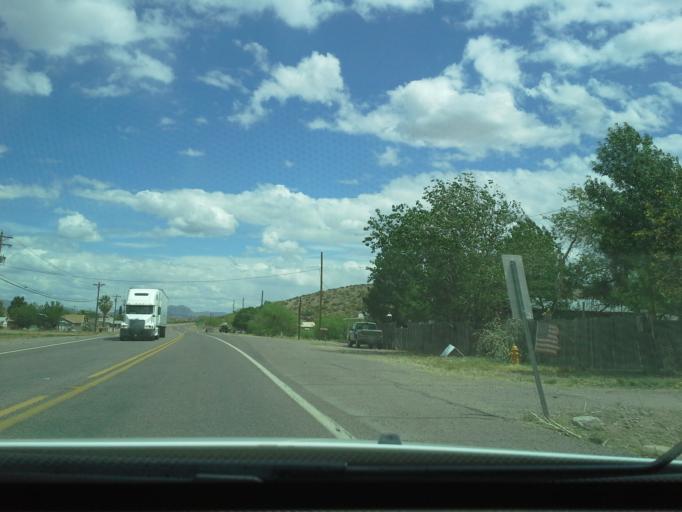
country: US
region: Arizona
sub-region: Graham County
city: Safford
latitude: 32.8127
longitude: -109.6010
